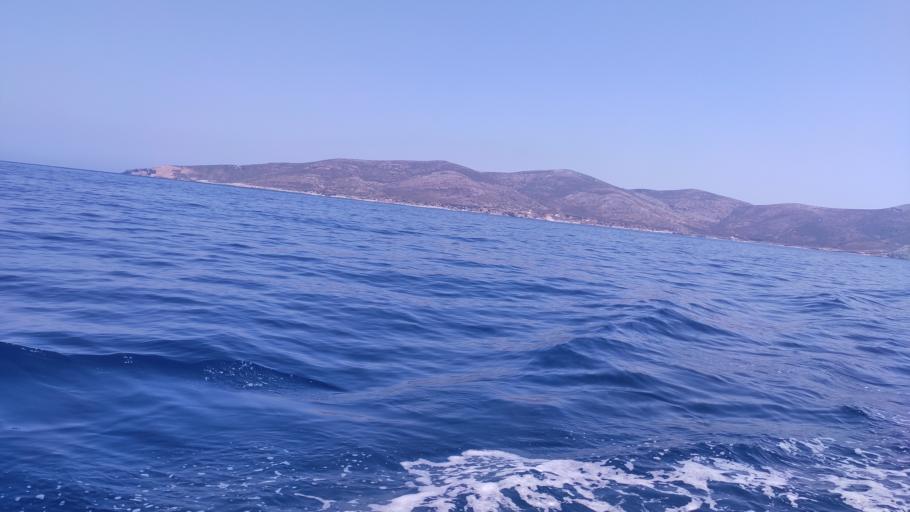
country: GR
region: South Aegean
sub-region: Nomos Dodekanisou
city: Pylion
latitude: 36.9319
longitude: 27.1010
